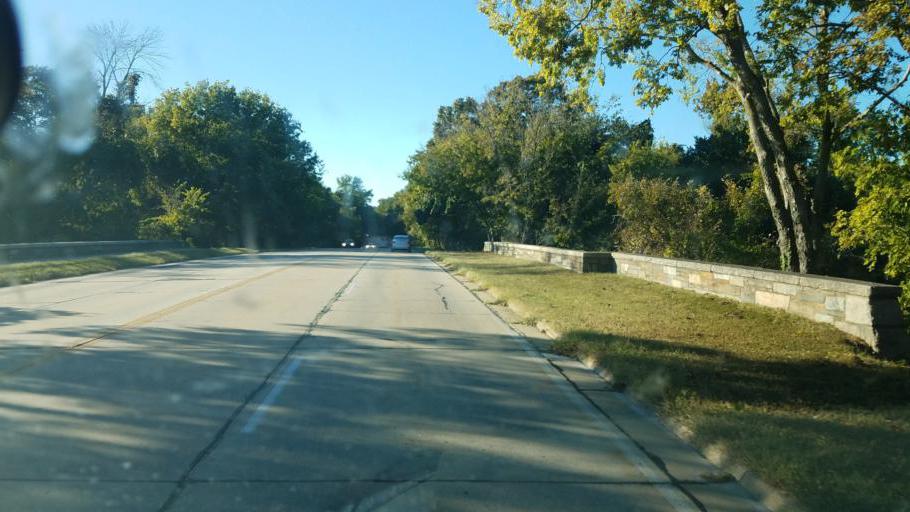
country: US
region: Virginia
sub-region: Fairfax County
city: Fort Hunt
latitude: 38.7128
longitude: -77.0737
